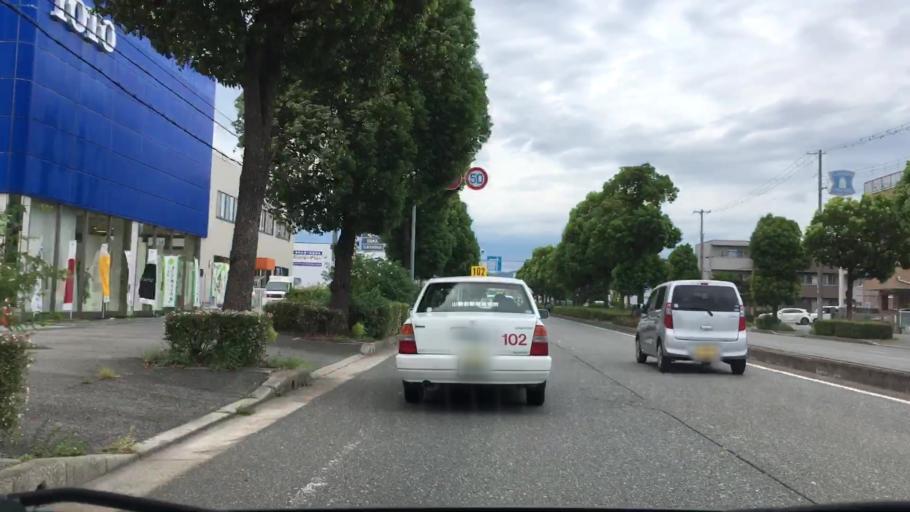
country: JP
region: Hyogo
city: Himeji
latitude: 34.8115
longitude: 134.6918
